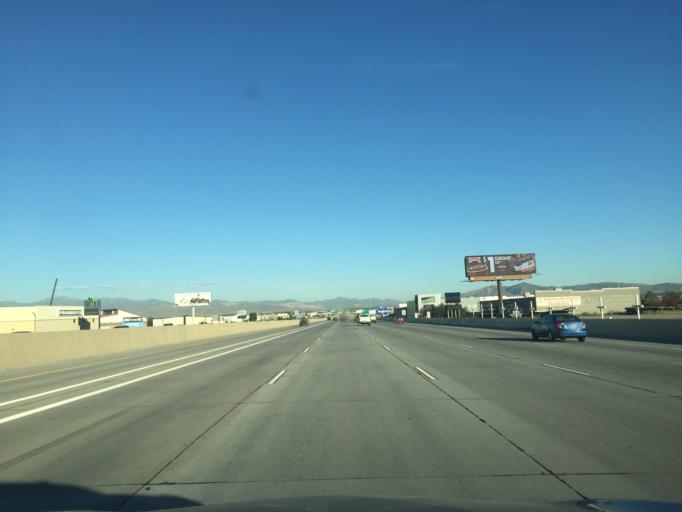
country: US
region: Utah
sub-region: Utah County
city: Lindon
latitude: 40.3349
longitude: -111.7451
